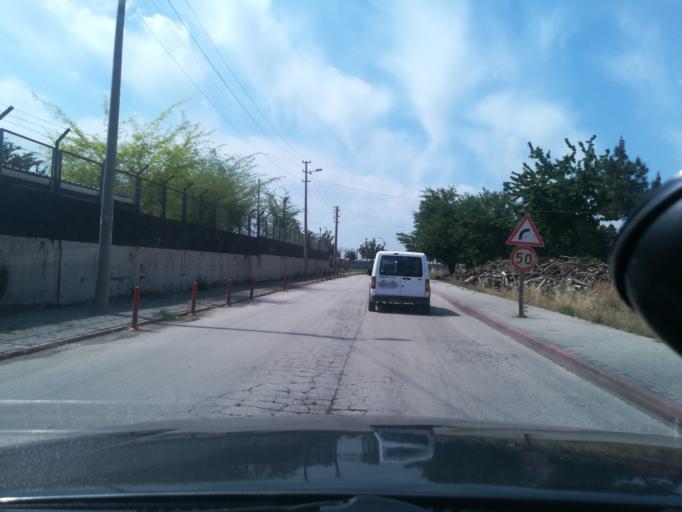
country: TR
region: Adana
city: Seyhan
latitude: 36.9879
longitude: 35.2862
